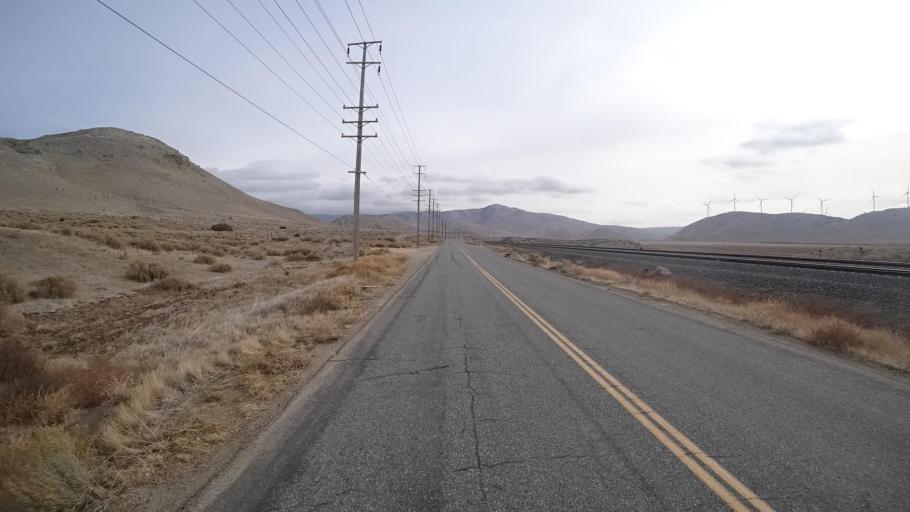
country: US
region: California
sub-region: Kern County
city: Tehachapi
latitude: 35.1212
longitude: -118.3573
